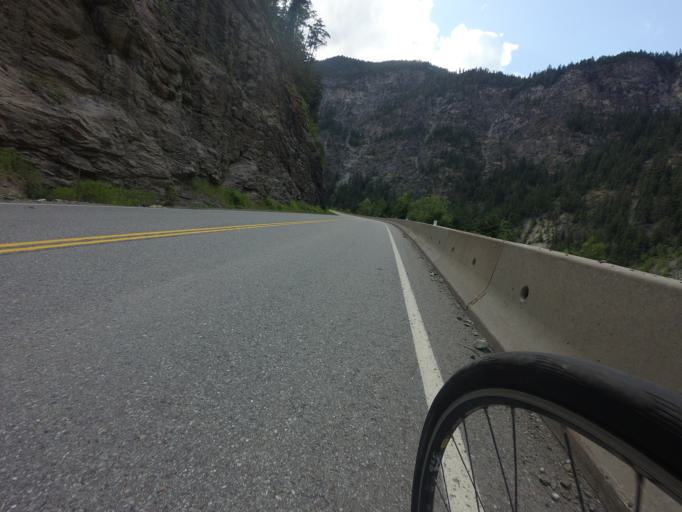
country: CA
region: British Columbia
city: Lillooet
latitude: 50.6461
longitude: -122.0648
